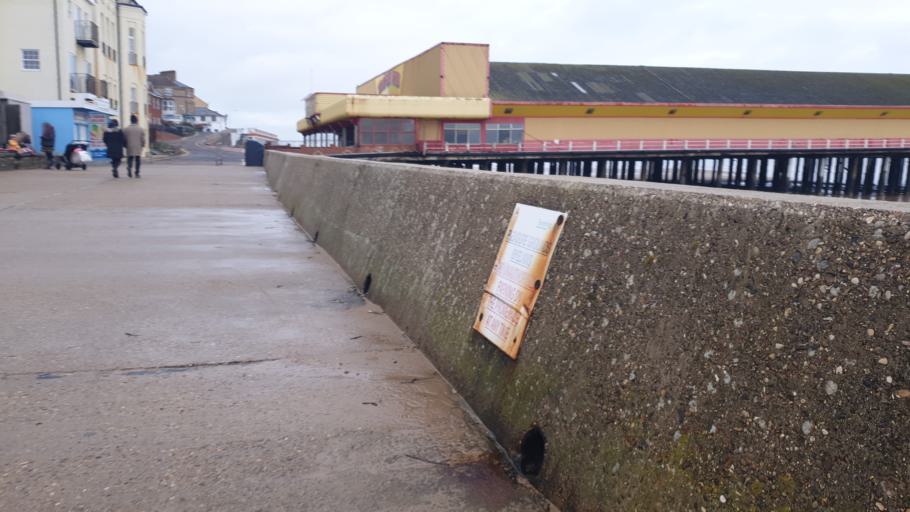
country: GB
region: England
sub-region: Essex
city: Walton-on-the-Naze
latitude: 51.8461
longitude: 1.2706
